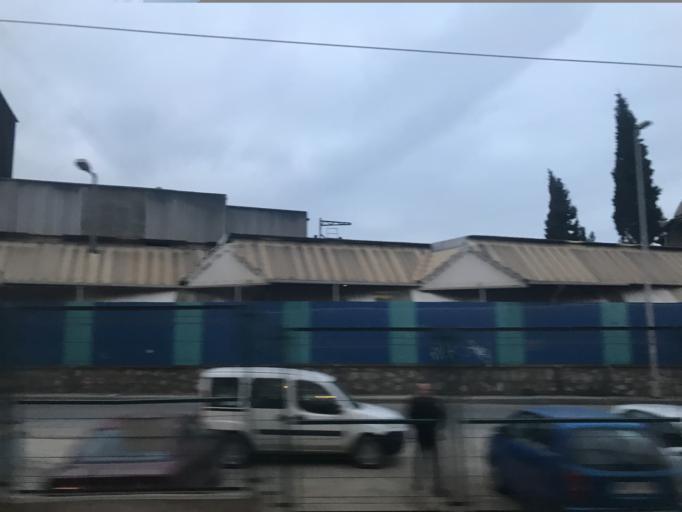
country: TR
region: Kocaeli
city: Darica
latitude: 40.7994
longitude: 29.3796
